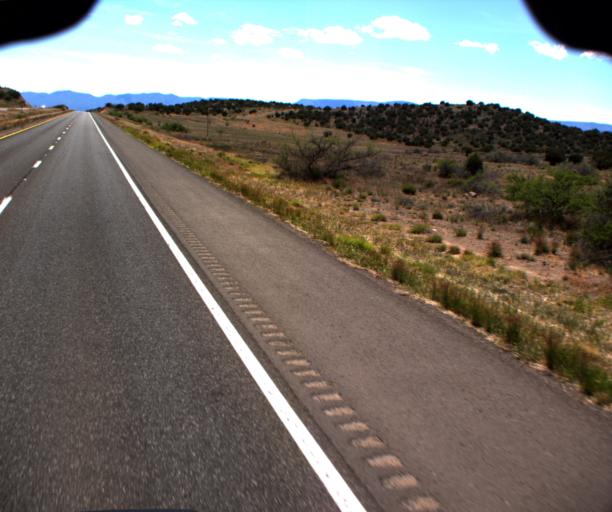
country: US
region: Arizona
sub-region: Yavapai County
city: Cornville
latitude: 34.8098
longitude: -111.9080
